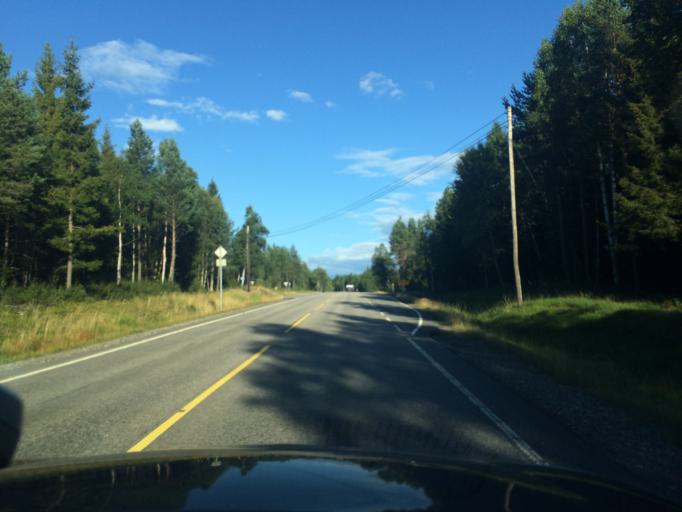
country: NO
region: Hedmark
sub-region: Elverum
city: Elverum
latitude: 61.0116
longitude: 11.8082
